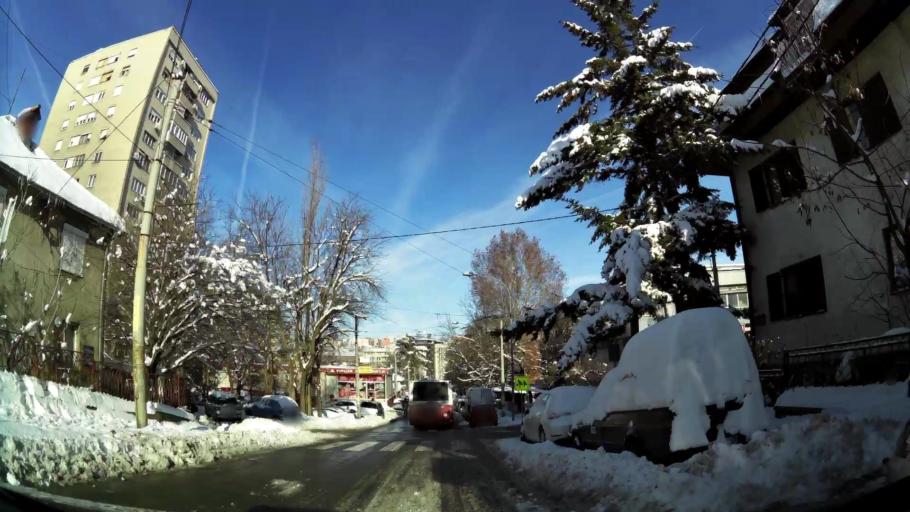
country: RS
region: Central Serbia
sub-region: Belgrade
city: Palilula
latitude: 44.7858
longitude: 20.5064
